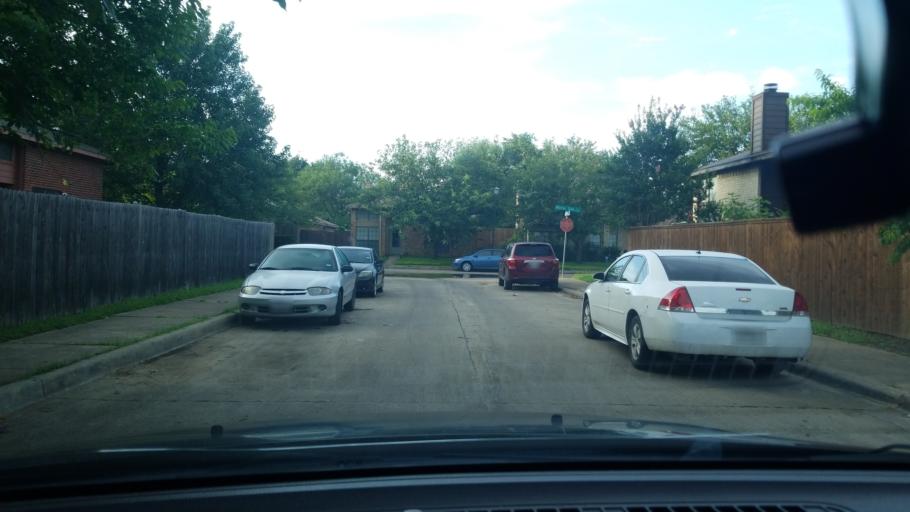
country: US
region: Texas
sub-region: Dallas County
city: Balch Springs
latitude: 32.7562
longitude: -96.6420
